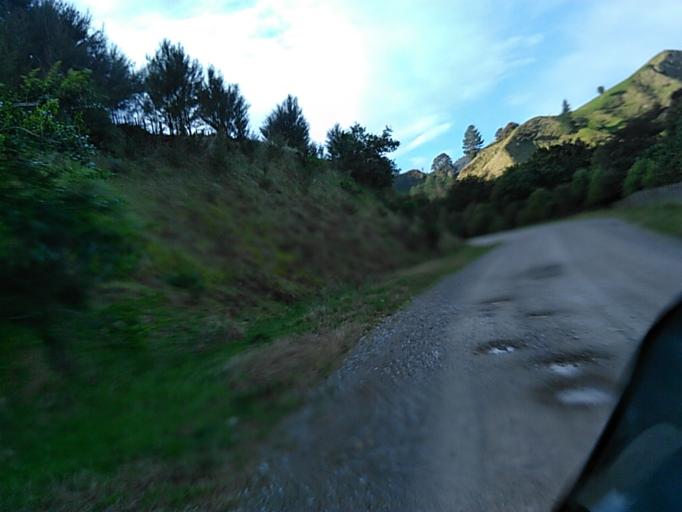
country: NZ
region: Gisborne
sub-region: Gisborne District
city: Gisborne
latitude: -38.6045
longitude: 178.0634
